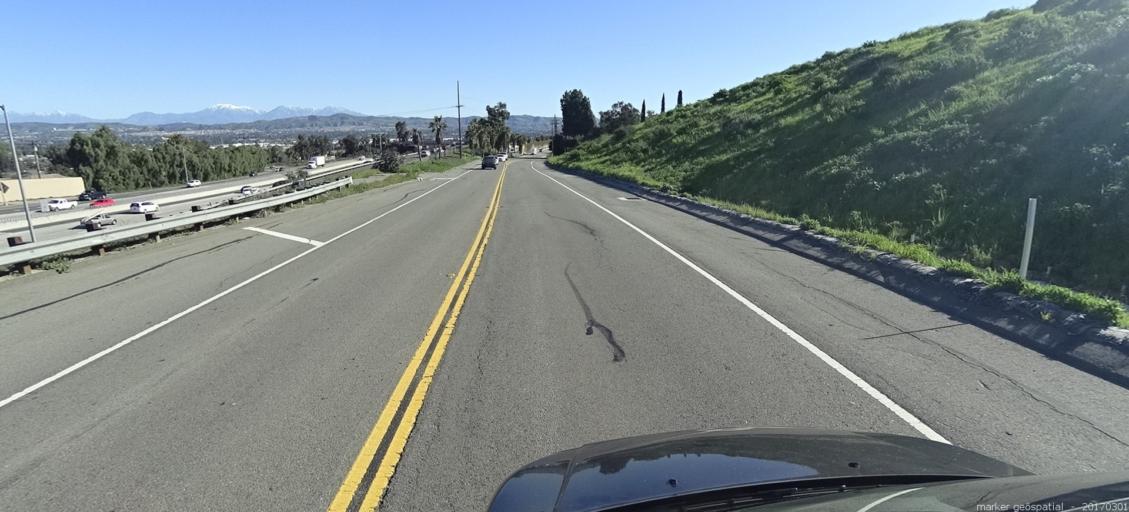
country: US
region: California
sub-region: Orange County
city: Villa Park
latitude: 33.8409
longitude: -117.8313
